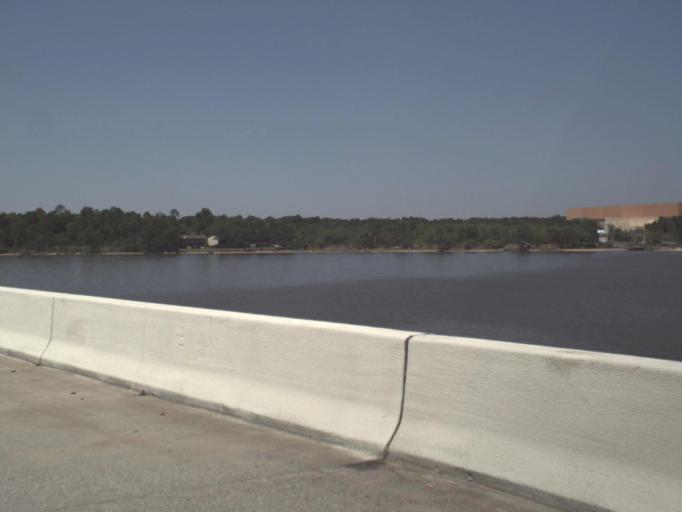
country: US
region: Florida
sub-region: Escambia County
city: Ferry Pass
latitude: 30.5108
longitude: -87.1562
